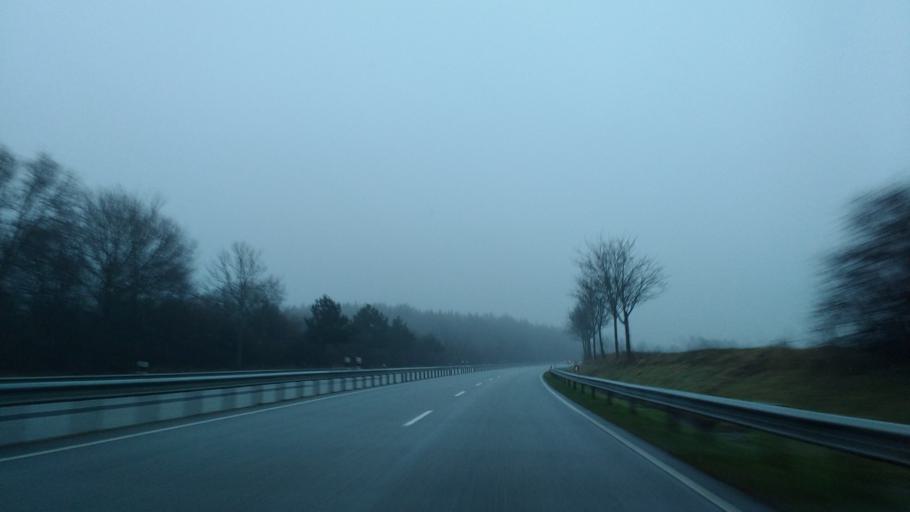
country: DE
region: Schleswig-Holstein
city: Jevenstedt
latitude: 54.2367
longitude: 9.6775
